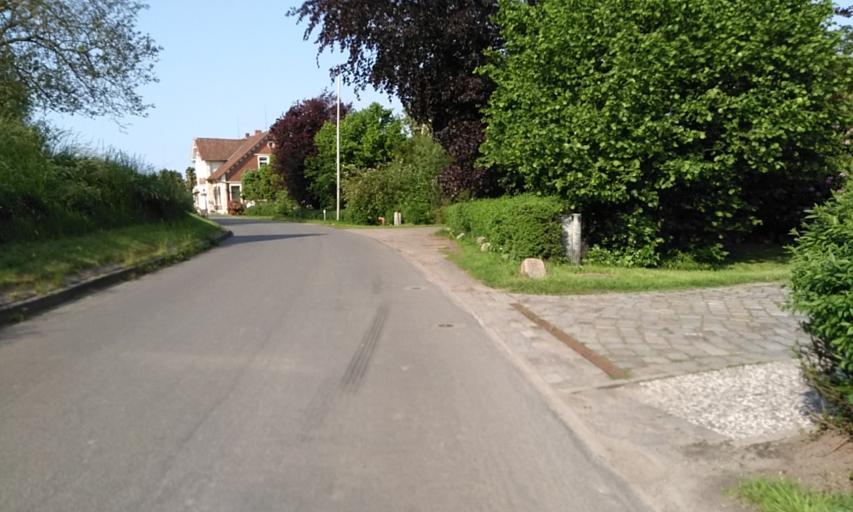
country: DE
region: Lower Saxony
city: Jork
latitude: 53.5052
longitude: 9.7336
